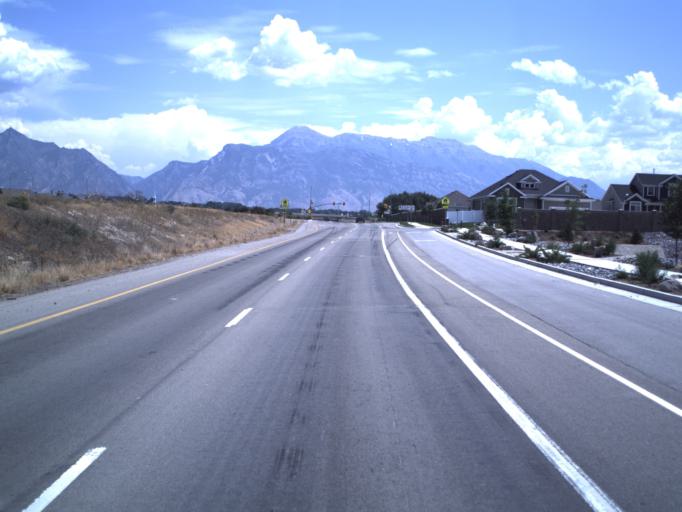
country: US
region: Utah
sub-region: Utah County
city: Lehi
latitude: 40.4124
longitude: -111.8907
